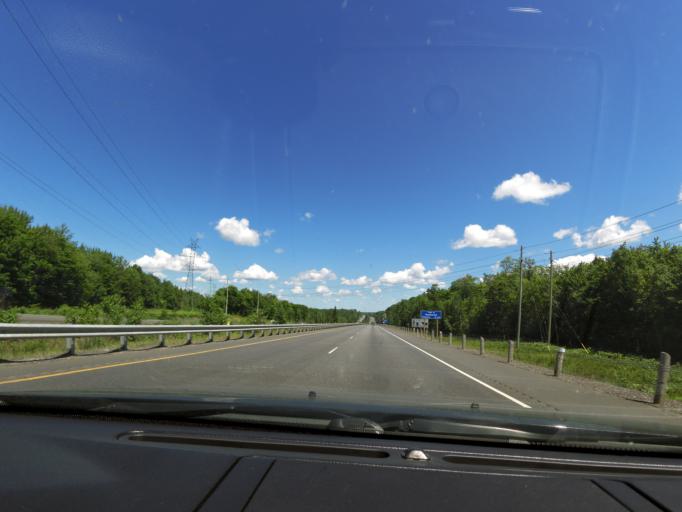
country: CA
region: Ontario
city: Bracebridge
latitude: 45.1584
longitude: -79.3113
